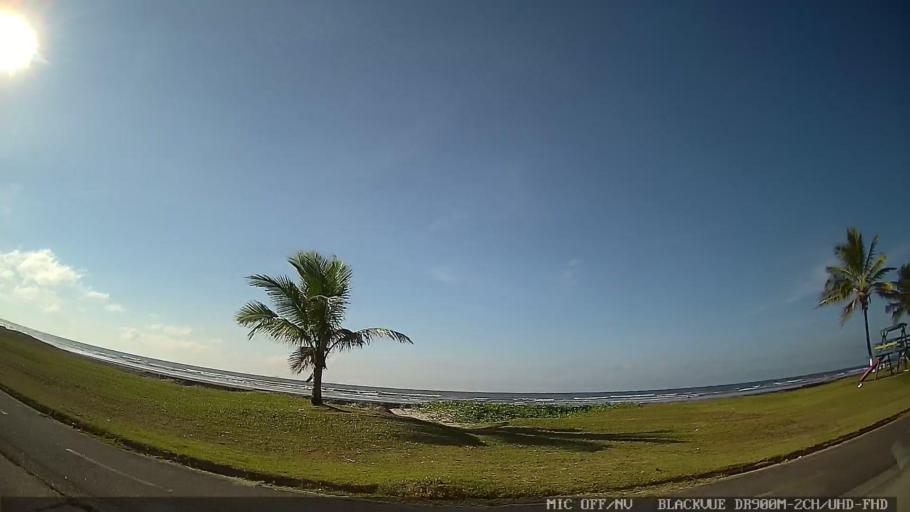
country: BR
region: Sao Paulo
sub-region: Peruibe
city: Peruibe
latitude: -24.2841
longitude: -46.9475
